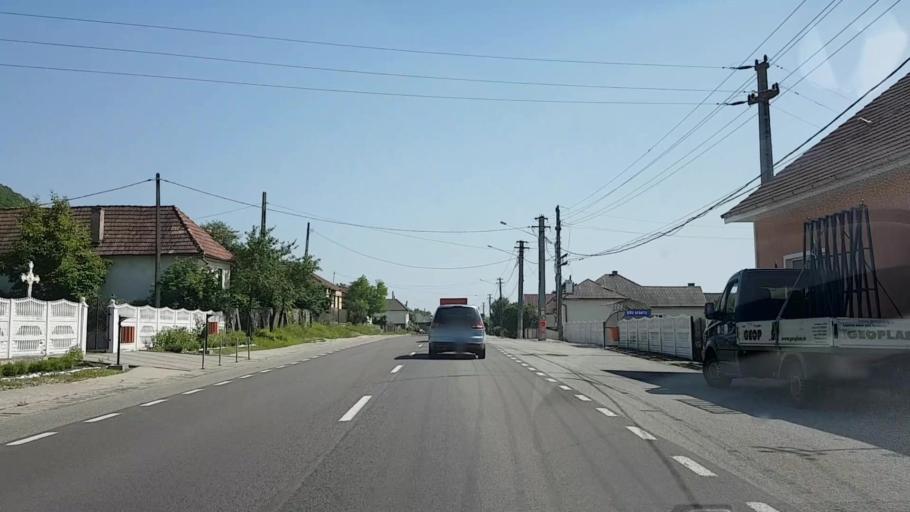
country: RO
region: Bistrita-Nasaud
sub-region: Comuna Sieu-Odorhei
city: Sieu-Odorhei
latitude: 47.1446
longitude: 24.3065
